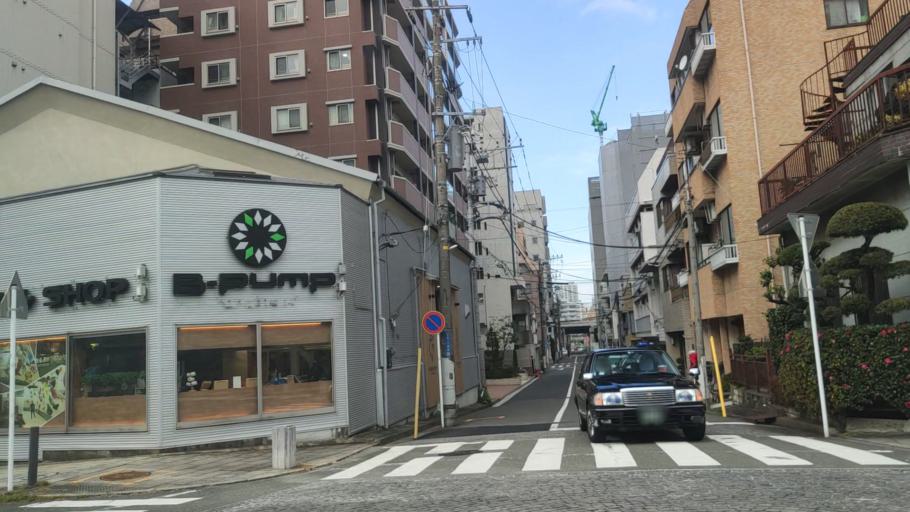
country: JP
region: Kanagawa
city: Yokohama
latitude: 35.4589
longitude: 139.6212
